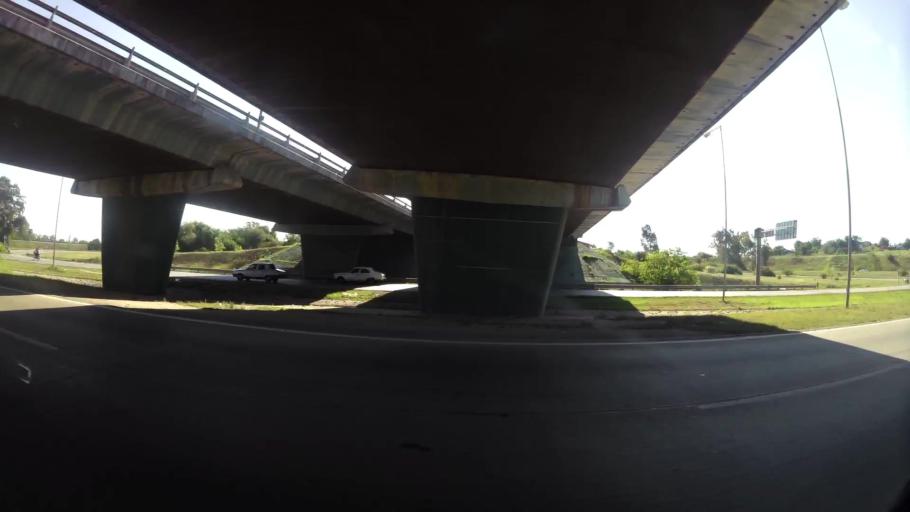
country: AR
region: Cordoba
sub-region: Departamento de Capital
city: Cordoba
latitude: -31.3974
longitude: -64.1275
